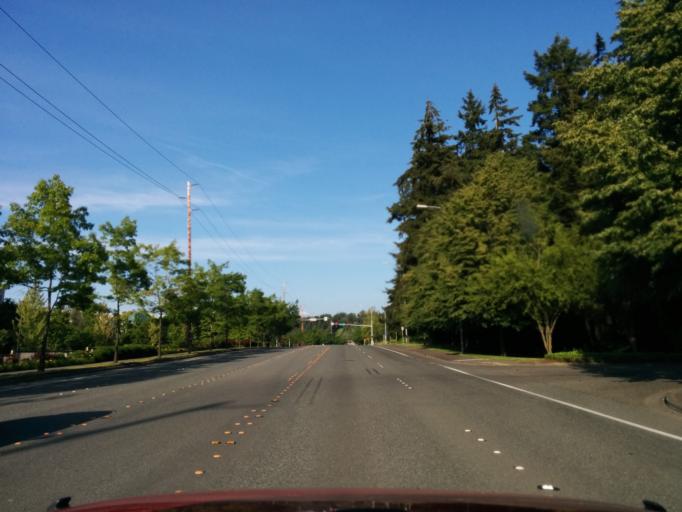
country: US
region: Washington
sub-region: King County
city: Redmond
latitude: 47.6763
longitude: -122.0959
